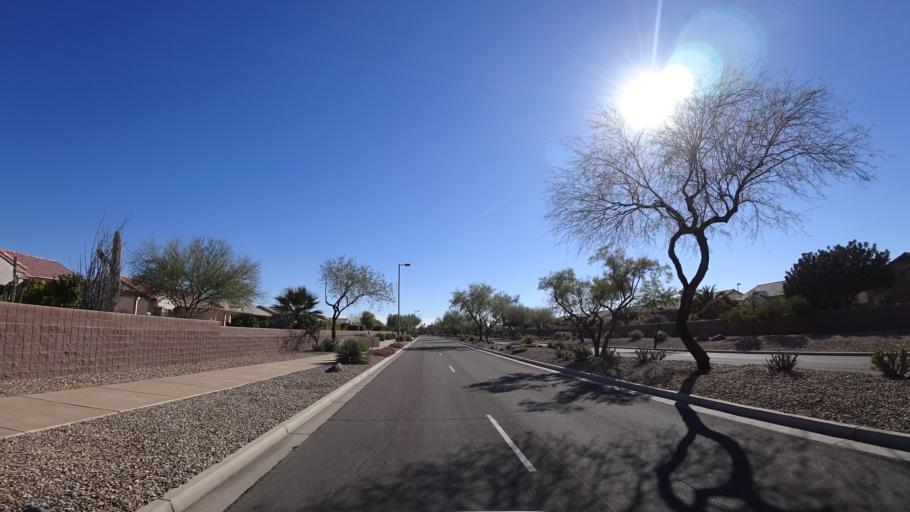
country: US
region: Arizona
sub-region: Maricopa County
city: Sun City West
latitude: 33.6498
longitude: -112.4125
